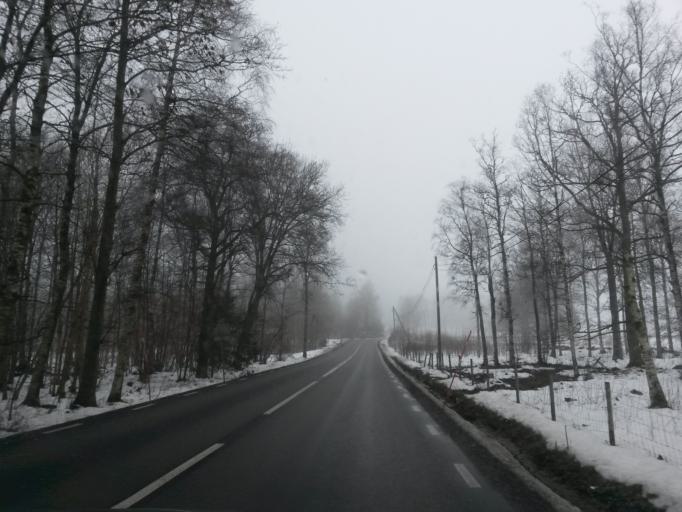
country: SE
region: Vaestra Goetaland
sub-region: Boras Kommun
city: Dalsjofors
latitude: 57.6975
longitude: 13.0605
